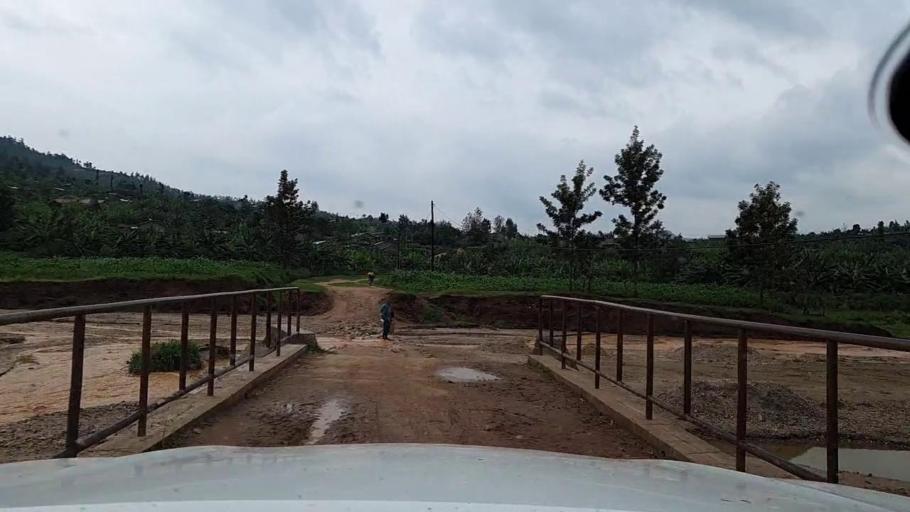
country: RW
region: Kigali
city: Kigali
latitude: -1.8783
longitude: 29.9268
